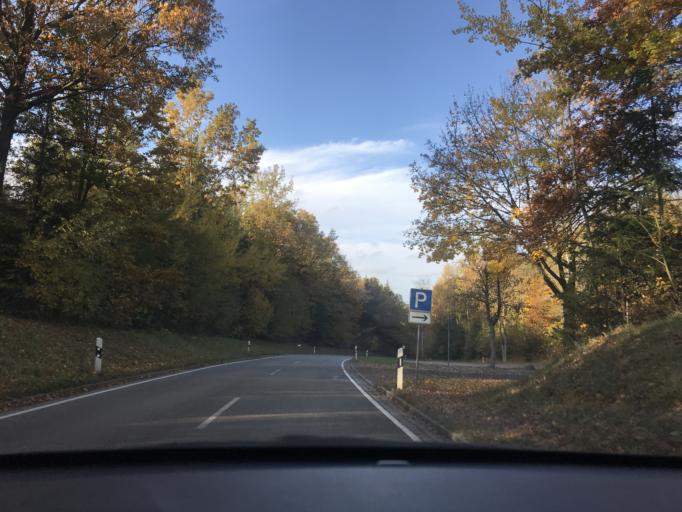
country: DE
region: Bavaria
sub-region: Lower Bavaria
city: Bad Abbach
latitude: 48.9486
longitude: 12.0827
